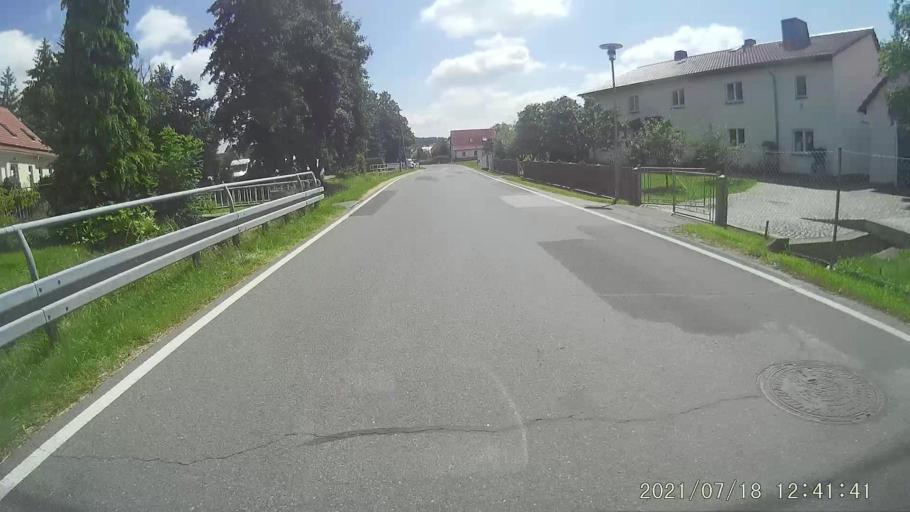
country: DE
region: Saxony
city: Konigshain
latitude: 51.1854
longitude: 14.8504
